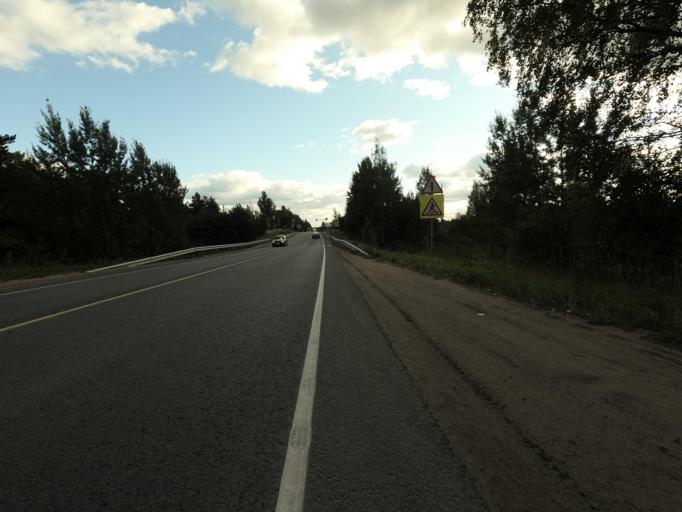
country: RU
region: Leningrad
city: Vsevolozhsk
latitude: 59.9822
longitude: 30.6543
